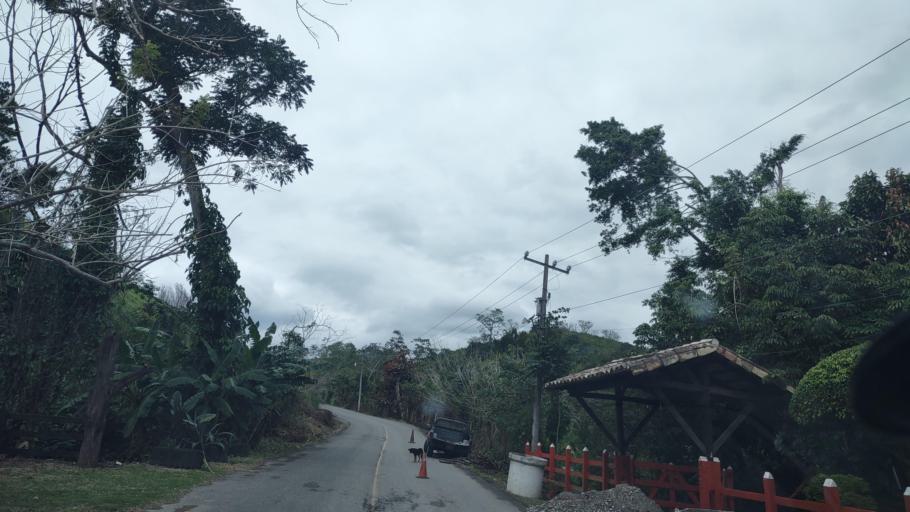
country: MX
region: Veracruz
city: Papantla de Olarte
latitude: 20.4445
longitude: -97.2904
